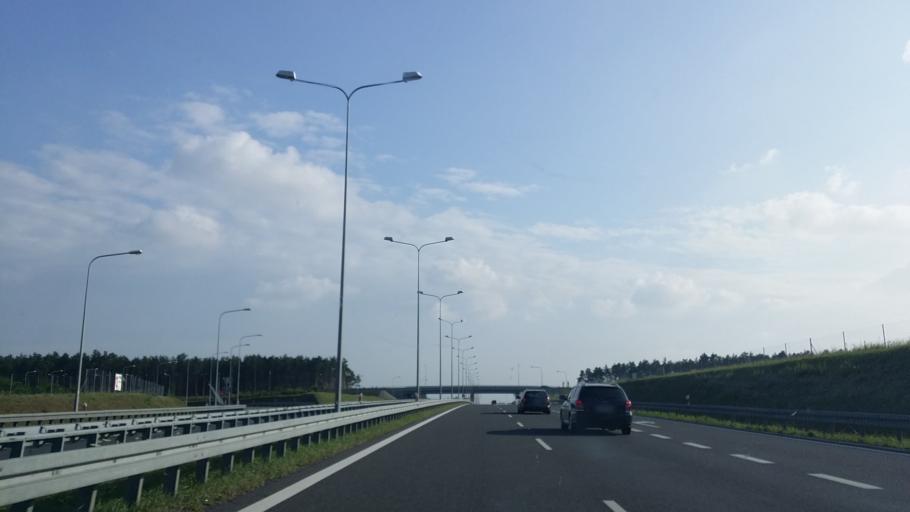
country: PL
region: Lubusz
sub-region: Powiat swiebodzinski
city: Swiebodzin
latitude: 52.3220
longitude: 15.5511
